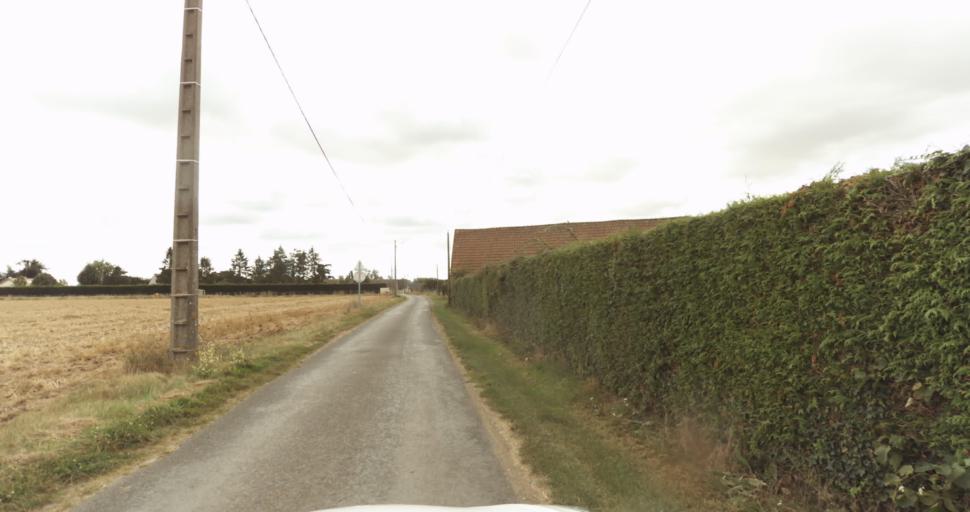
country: FR
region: Haute-Normandie
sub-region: Departement de l'Eure
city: Nonancourt
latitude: 48.7886
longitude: 1.1456
